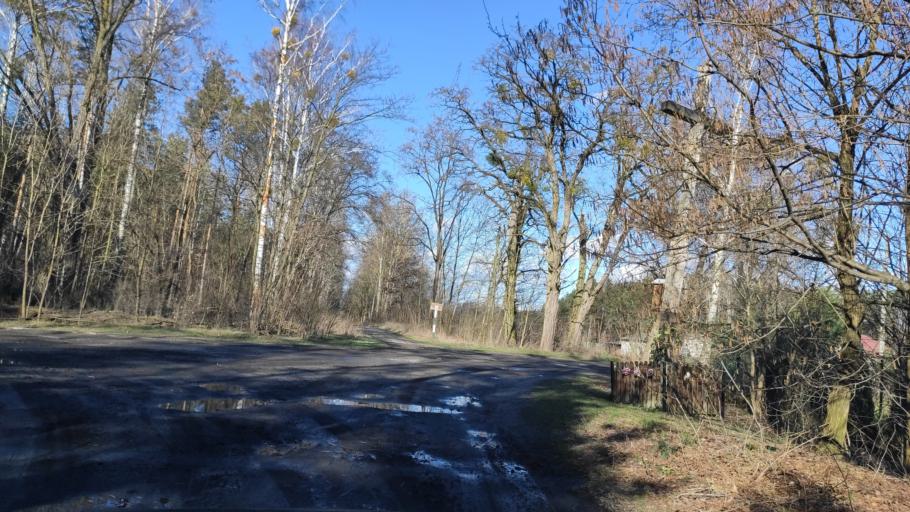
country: PL
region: Masovian Voivodeship
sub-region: Powiat radomski
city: Jedlnia-Letnisko
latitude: 51.4615
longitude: 21.3254
